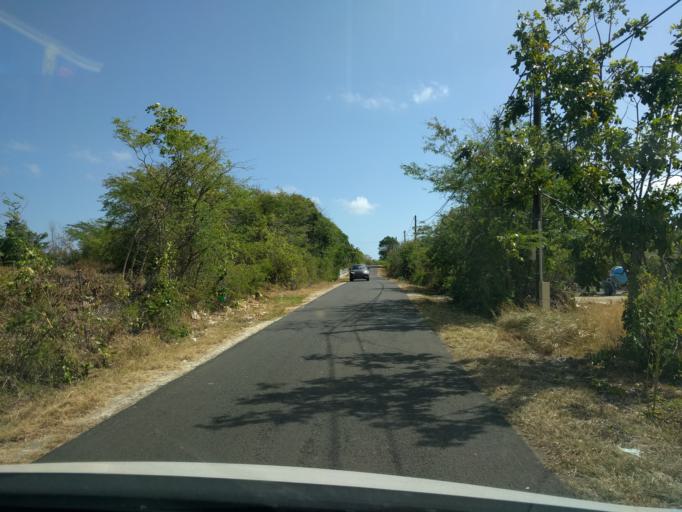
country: GP
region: Guadeloupe
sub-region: Guadeloupe
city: Grand-Bourg
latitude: 15.9777
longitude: -61.2472
